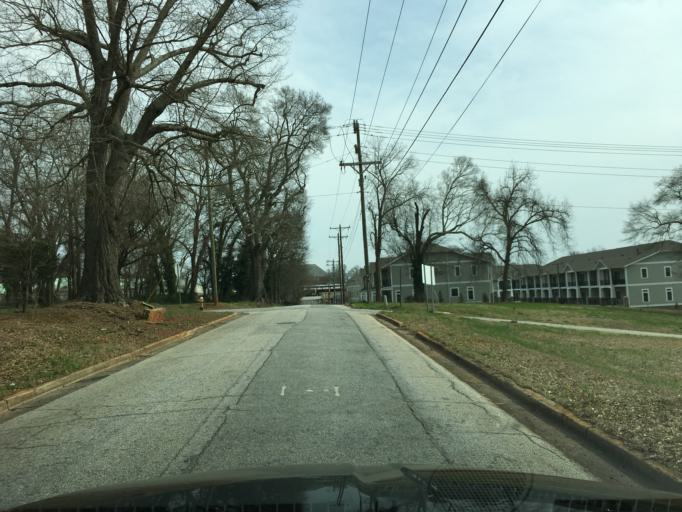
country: US
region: South Carolina
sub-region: Greenville County
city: Greenville
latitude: 34.8539
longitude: -82.4101
